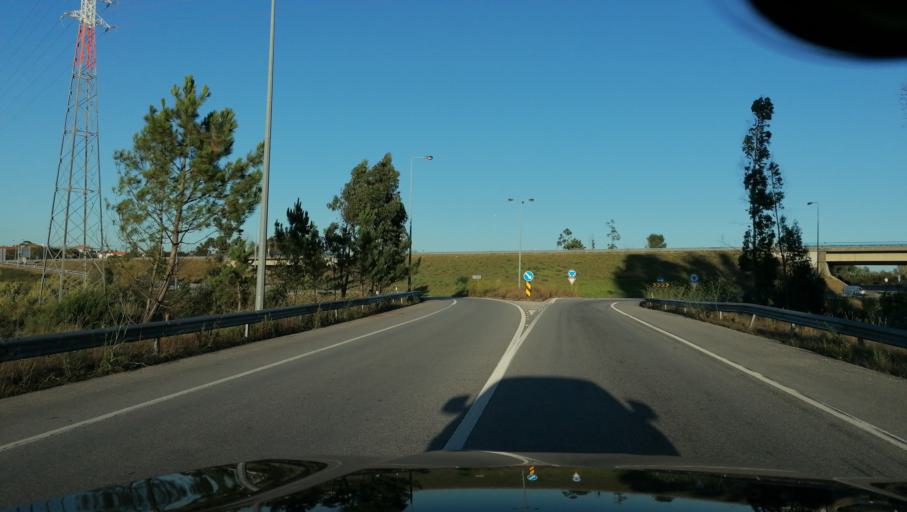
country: PT
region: Aveiro
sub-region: Aveiro
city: Oliveirinha
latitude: 40.5840
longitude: -8.6034
